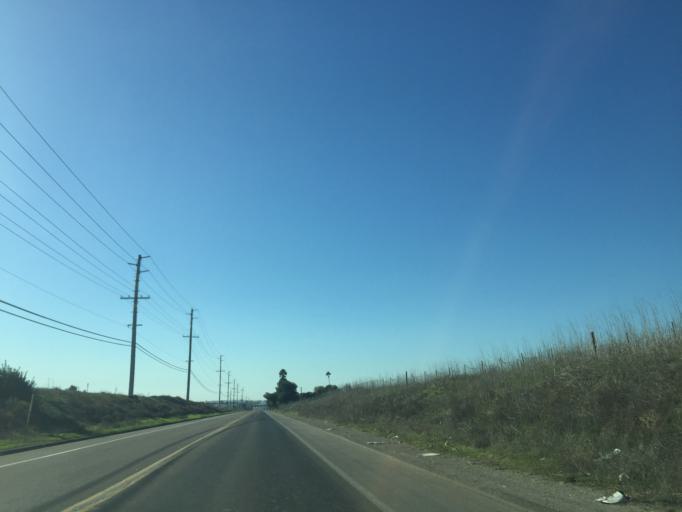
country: MX
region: Baja California
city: Tijuana
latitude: 32.5675
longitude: -116.9305
